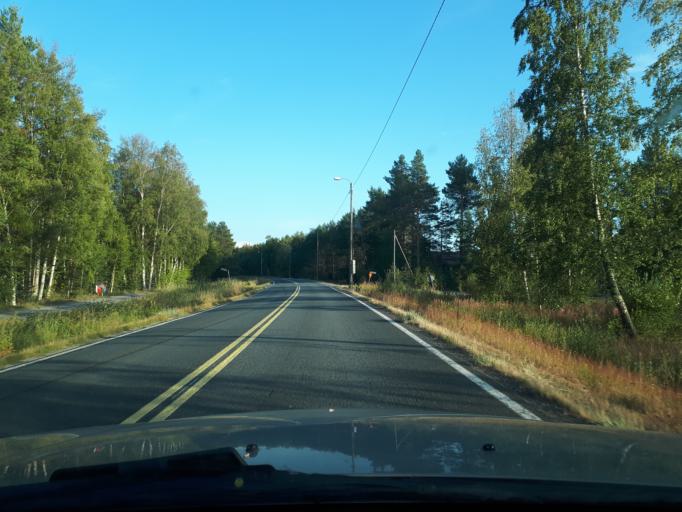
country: FI
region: Northern Ostrobothnia
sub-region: Oulu
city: Oulunsalo
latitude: 64.9885
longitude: 25.2583
